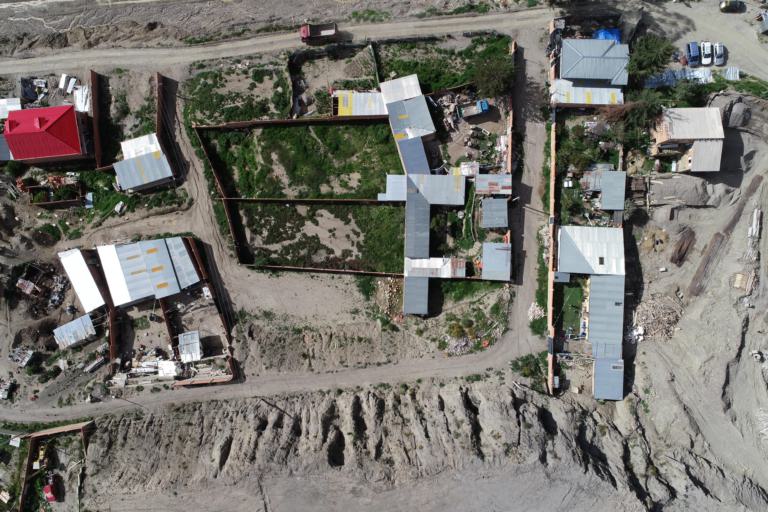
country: BO
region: La Paz
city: La Paz
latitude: -16.5030
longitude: -68.0766
